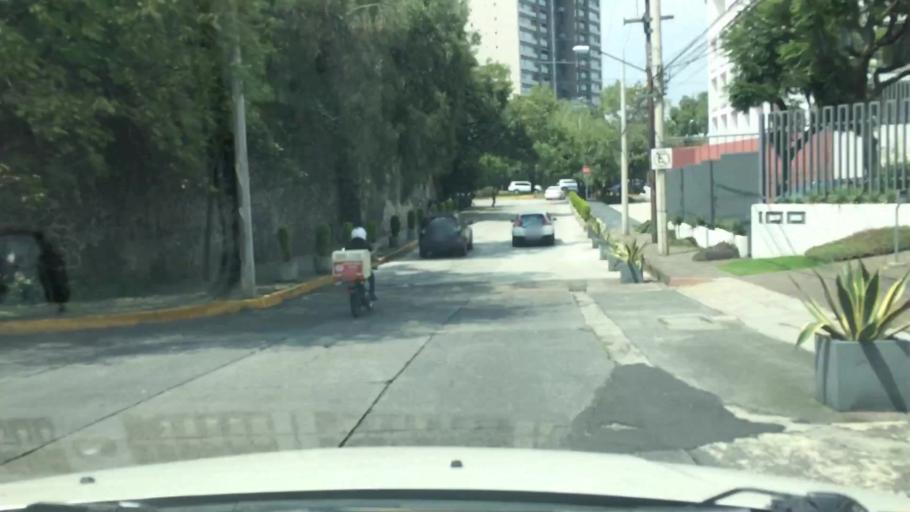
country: MX
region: Mexico City
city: Magdalena Contreras
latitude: 19.3319
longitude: -99.2041
